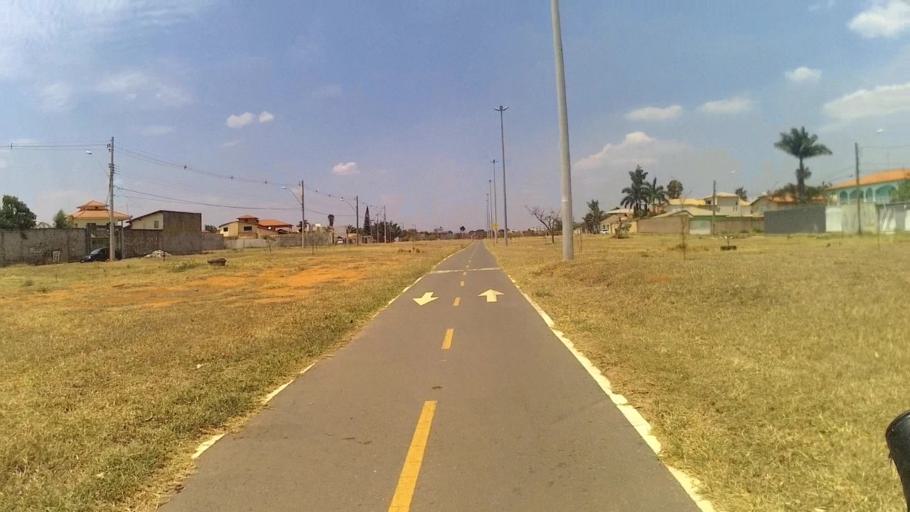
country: BR
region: Federal District
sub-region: Brasilia
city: Brasilia
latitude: -15.8718
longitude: -48.0562
